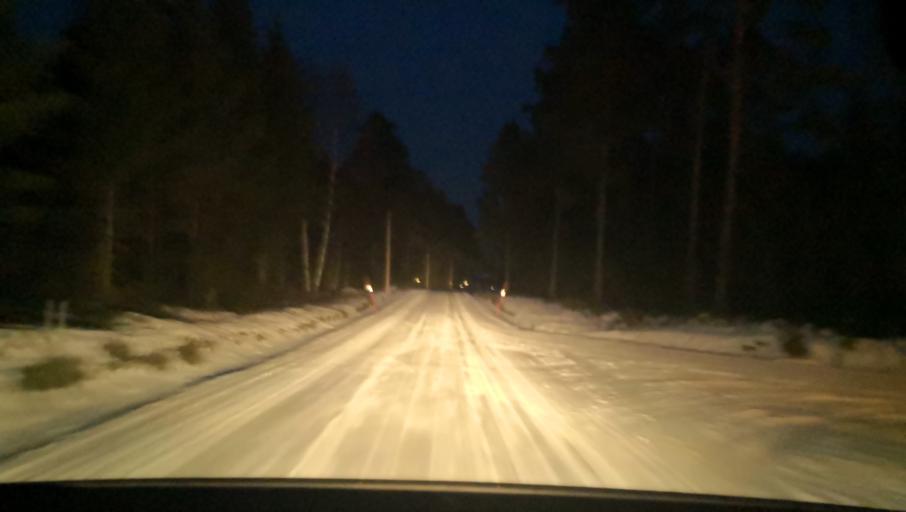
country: SE
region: Uppsala
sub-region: Heby Kommun
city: Tarnsjo
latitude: 60.2705
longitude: 16.7953
